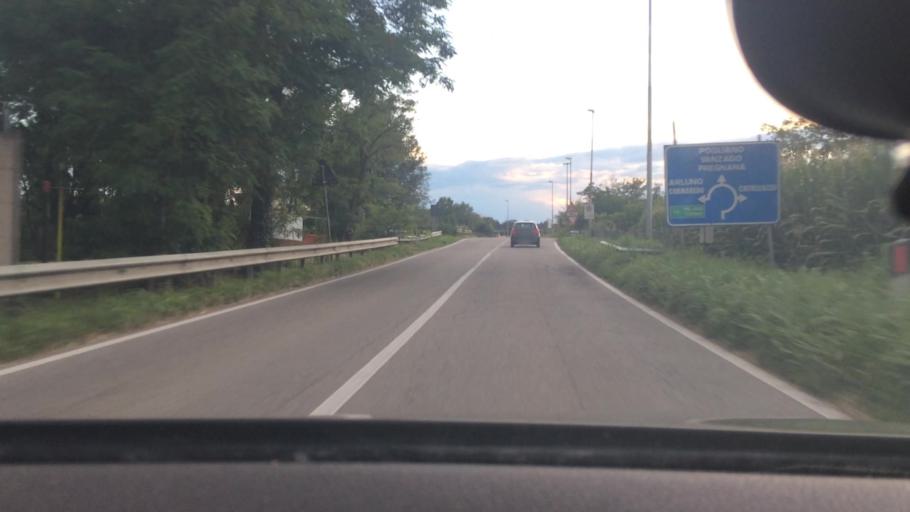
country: IT
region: Lombardy
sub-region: Citta metropolitana di Milano
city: Pregnana Milanese
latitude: 45.5198
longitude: 9.0204
